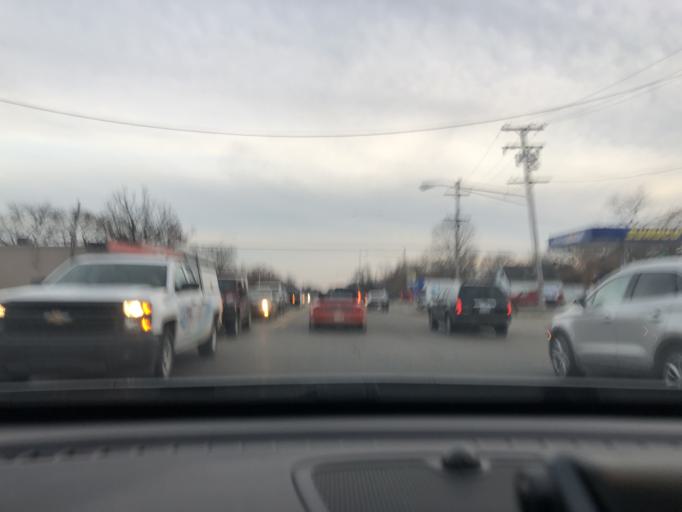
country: US
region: Michigan
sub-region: Wayne County
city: Allen Park
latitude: 42.2699
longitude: -83.2319
